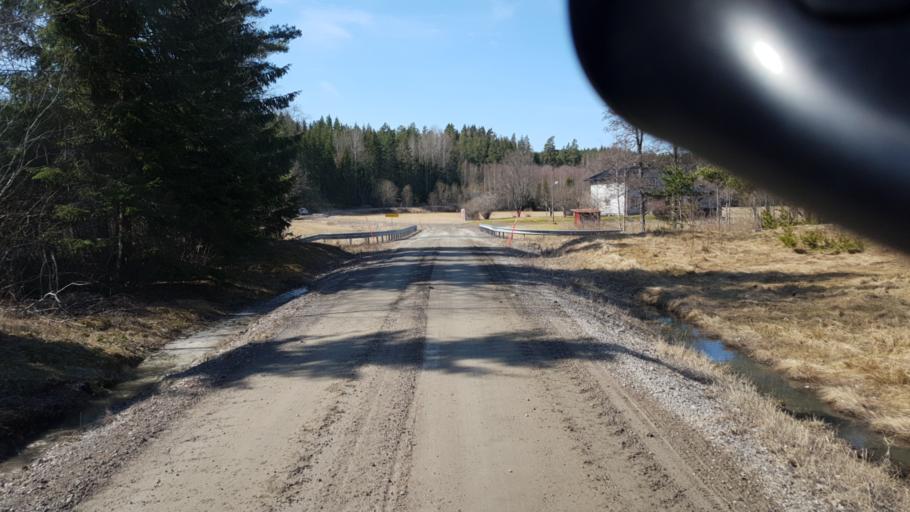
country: SE
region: Vaermland
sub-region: Grums Kommun
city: Grums
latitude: 59.5342
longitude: 12.9051
